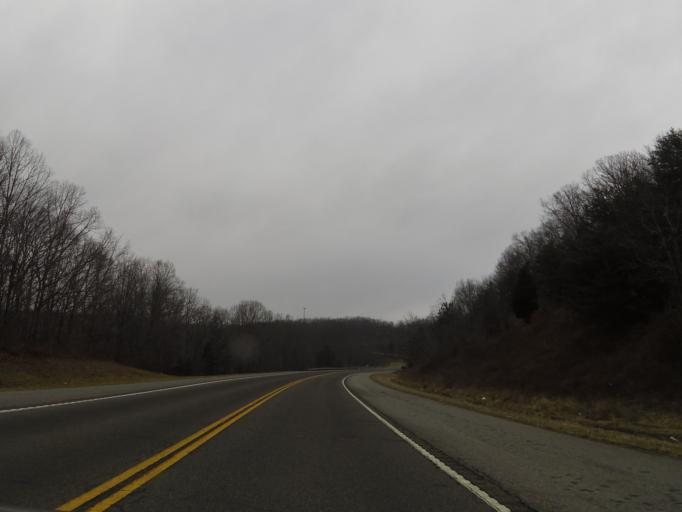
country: US
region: Tennessee
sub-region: Morgan County
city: Wartburg
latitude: 36.2161
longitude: -84.6658
